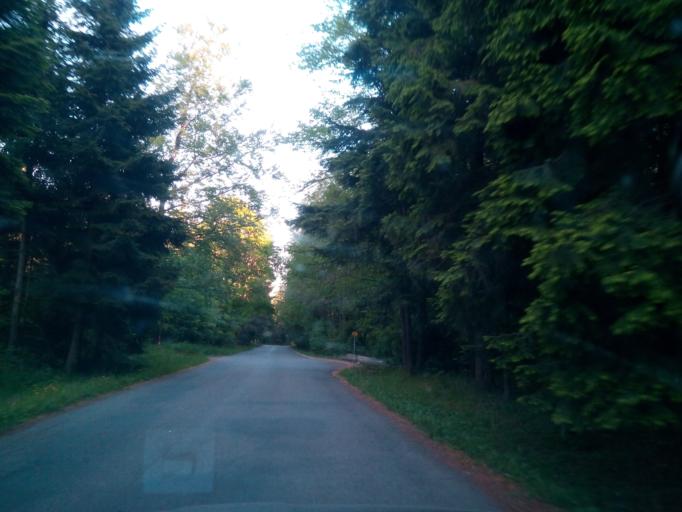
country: CZ
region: South Moravian
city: Ostrov u Macochy
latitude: 49.3713
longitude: 16.7328
